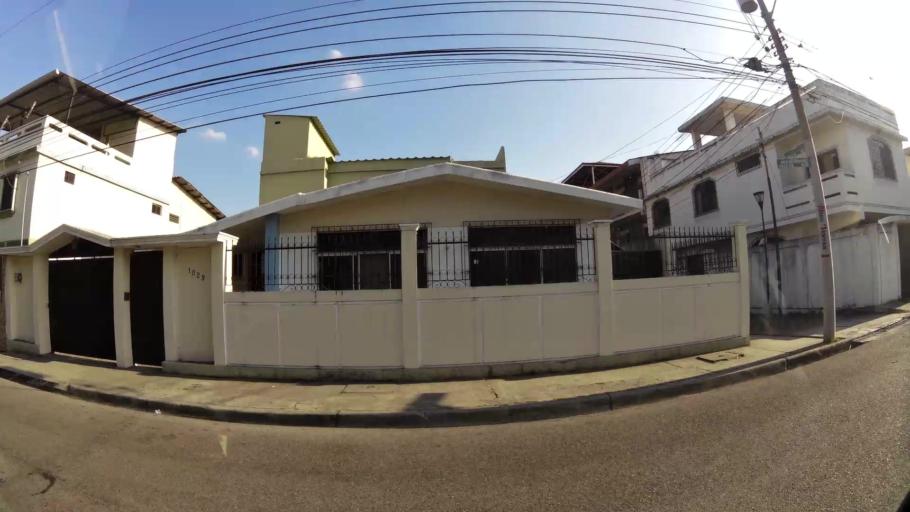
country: EC
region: Guayas
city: Guayaquil
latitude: -2.1612
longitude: -79.9129
